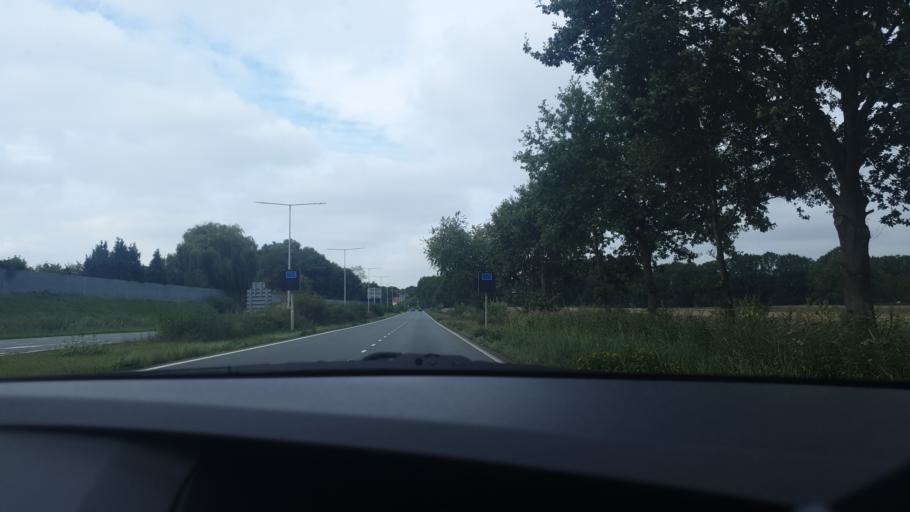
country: NL
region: North Brabant
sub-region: Gemeente Bergen op Zoom
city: Bergen op Zoom
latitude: 51.5120
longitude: 4.3015
